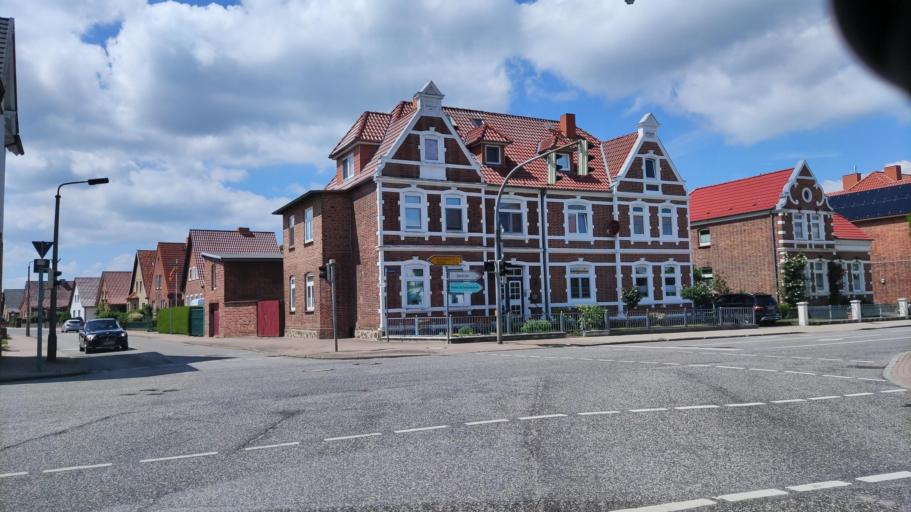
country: DE
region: Mecklenburg-Vorpommern
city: Wittenburg
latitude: 53.5068
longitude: 11.0783
